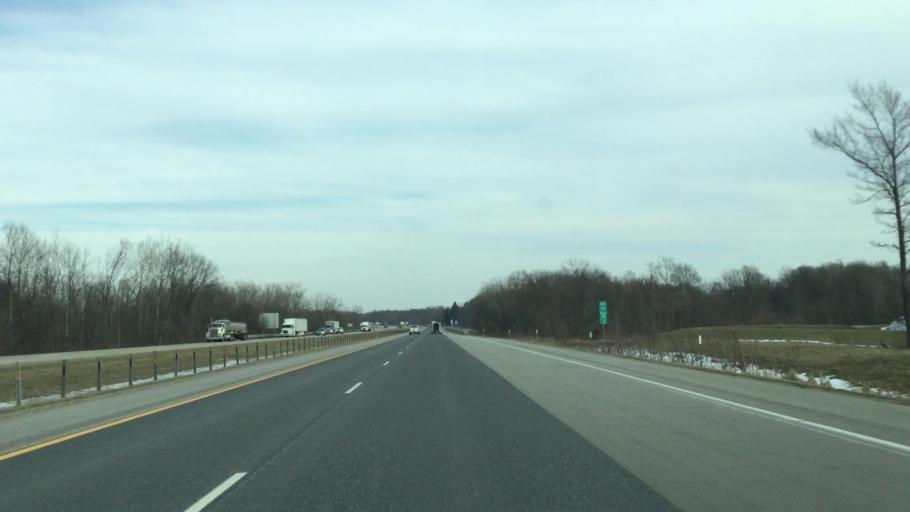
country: US
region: Michigan
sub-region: Berrien County
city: Watervliet
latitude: 42.1785
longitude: -86.2541
